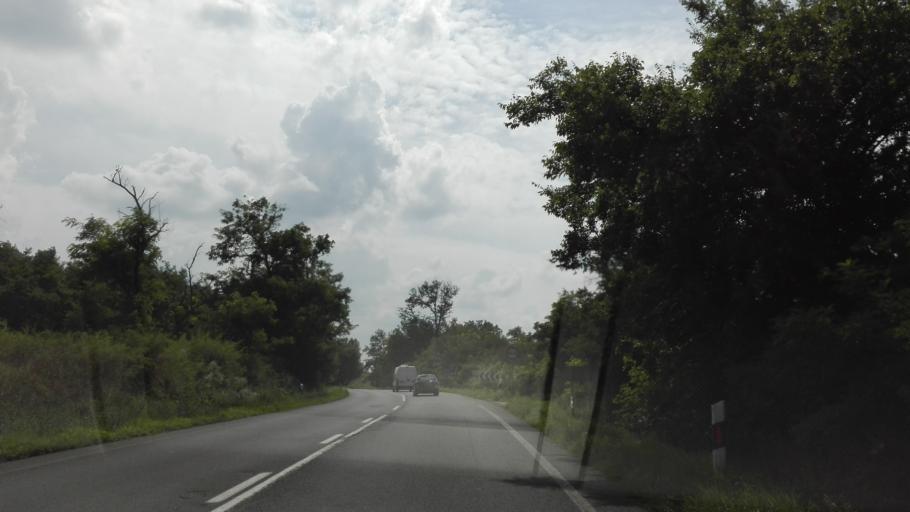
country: HU
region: Fejer
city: Alap
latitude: 46.7784
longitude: 18.6699
